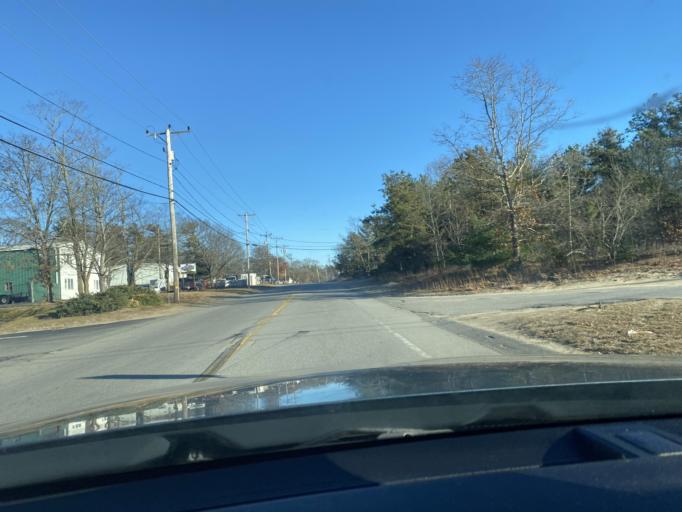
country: US
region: Massachusetts
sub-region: Plymouth County
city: Wareham Center
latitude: 41.7696
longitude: -70.7020
